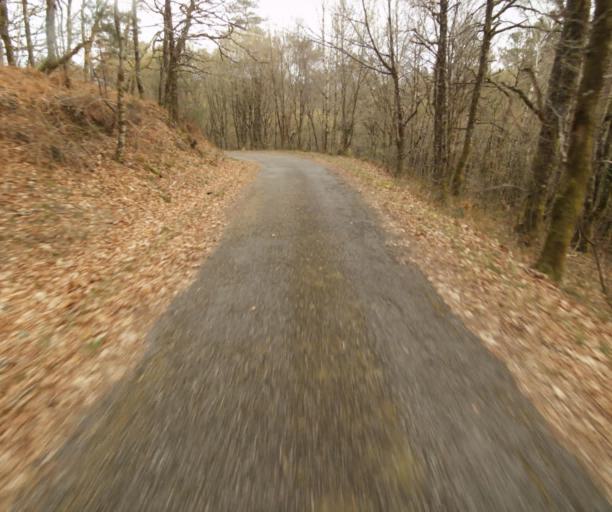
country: FR
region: Limousin
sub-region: Departement de la Correze
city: Argentat
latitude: 45.2079
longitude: 1.9914
